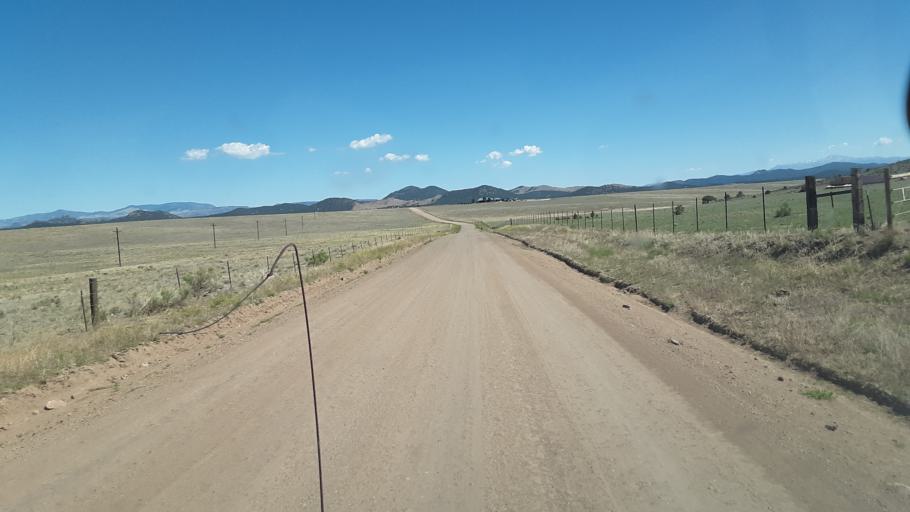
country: US
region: Colorado
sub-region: Custer County
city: Westcliffe
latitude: 38.2507
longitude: -105.4999
